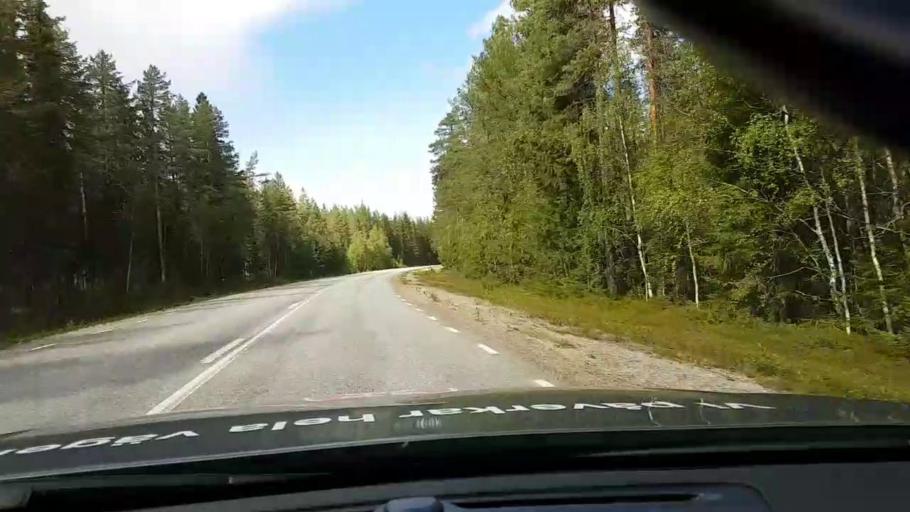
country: SE
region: Vaesternorrland
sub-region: OErnskoeldsviks Kommun
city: Bredbyn
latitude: 63.6042
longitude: 17.9029
